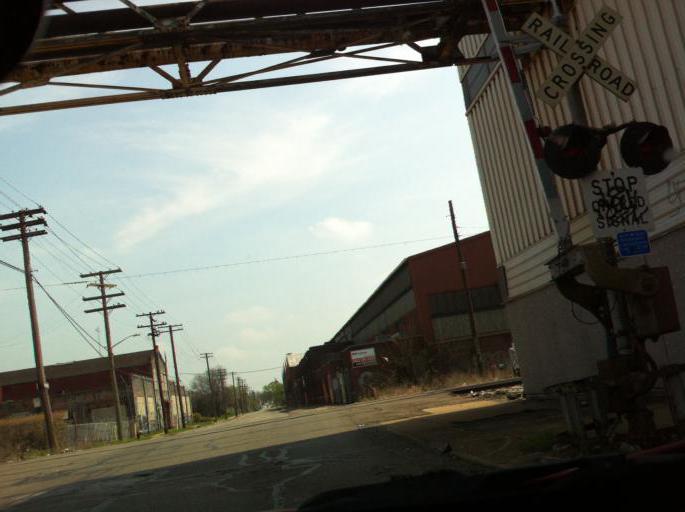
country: US
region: Michigan
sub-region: Wayne County
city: River Rouge
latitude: 42.3044
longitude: -83.1018
